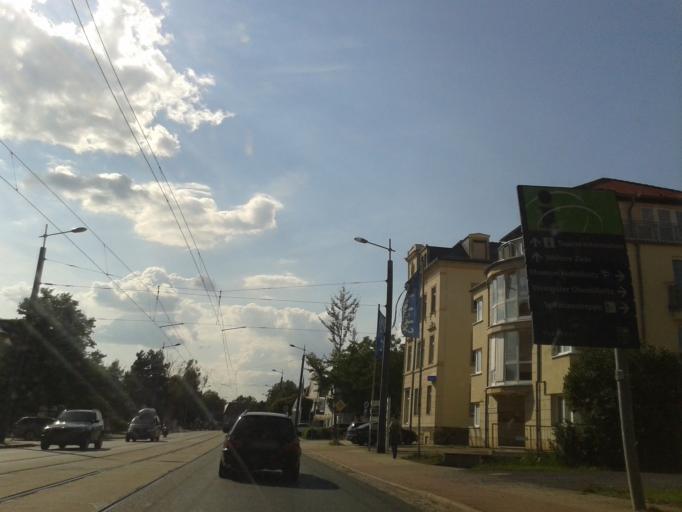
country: DE
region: Saxony
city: Radebeul
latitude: 51.1047
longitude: 13.6663
